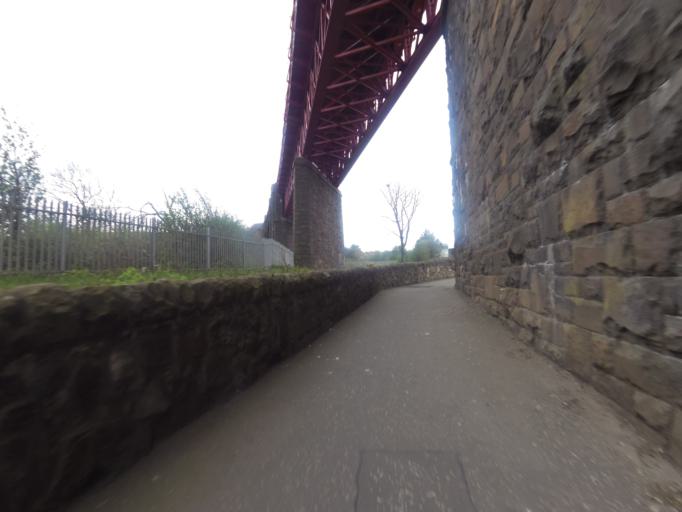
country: GB
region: Scotland
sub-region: Fife
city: Inverkeithing
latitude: 56.0223
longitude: -3.4052
